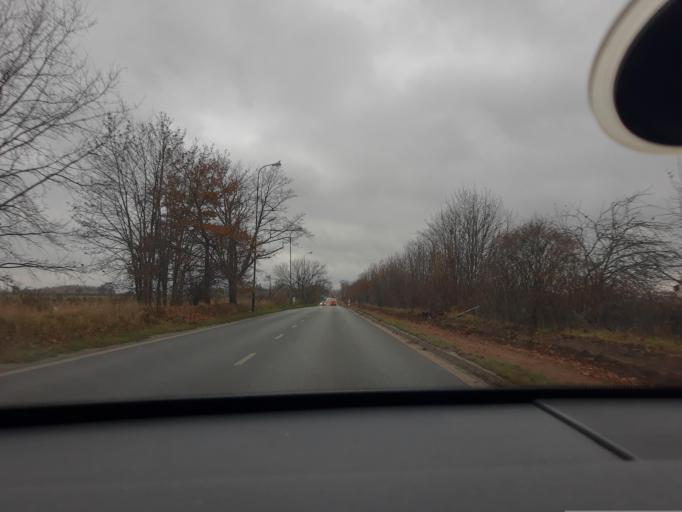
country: PL
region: Lodz Voivodeship
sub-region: Powiat pabianicki
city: Konstantynow Lodzki
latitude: 51.7570
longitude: 19.3922
